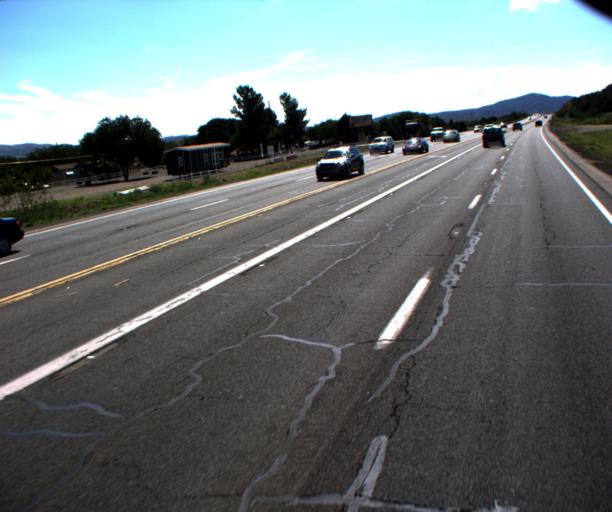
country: US
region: Arizona
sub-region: Yavapai County
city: Dewey-Humboldt
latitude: 34.5693
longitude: -112.2713
